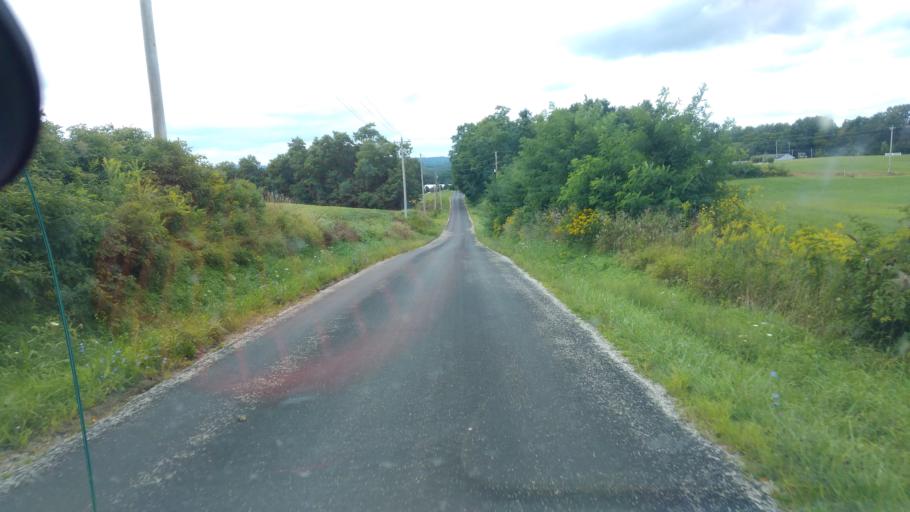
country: US
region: Ohio
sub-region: Ashland County
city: Ashland
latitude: 40.8220
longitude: -82.3857
